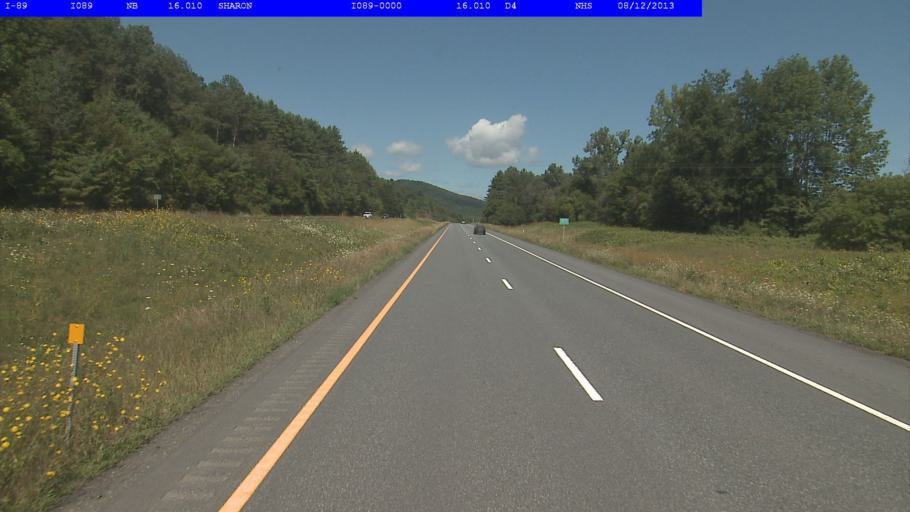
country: US
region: Vermont
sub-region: Windsor County
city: Woodstock
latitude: 43.7904
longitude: -72.4995
